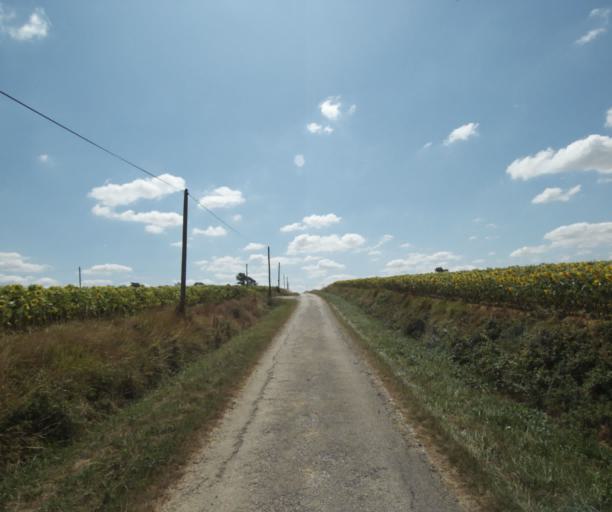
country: FR
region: Midi-Pyrenees
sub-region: Departement de la Haute-Garonne
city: Saint-Felix-Lauragais
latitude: 43.4666
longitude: 1.8407
